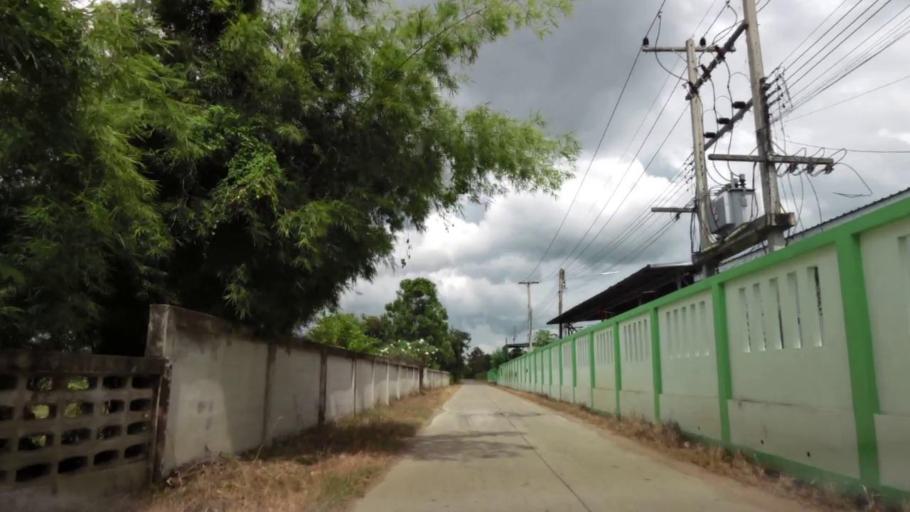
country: TH
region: Nakhon Sawan
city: Phai Sali
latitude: 15.6008
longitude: 100.6566
